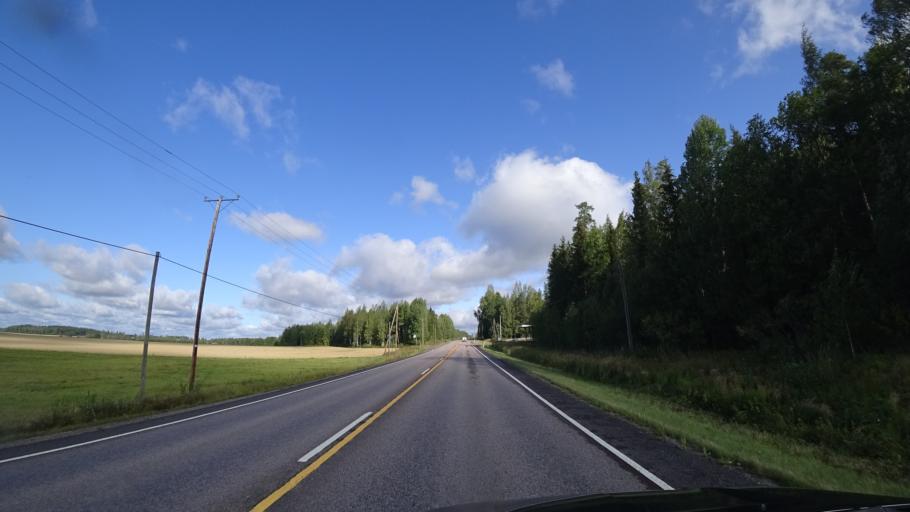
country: FI
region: Uusimaa
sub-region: Helsinki
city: Nurmijaervi
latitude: 60.5031
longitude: 24.9325
